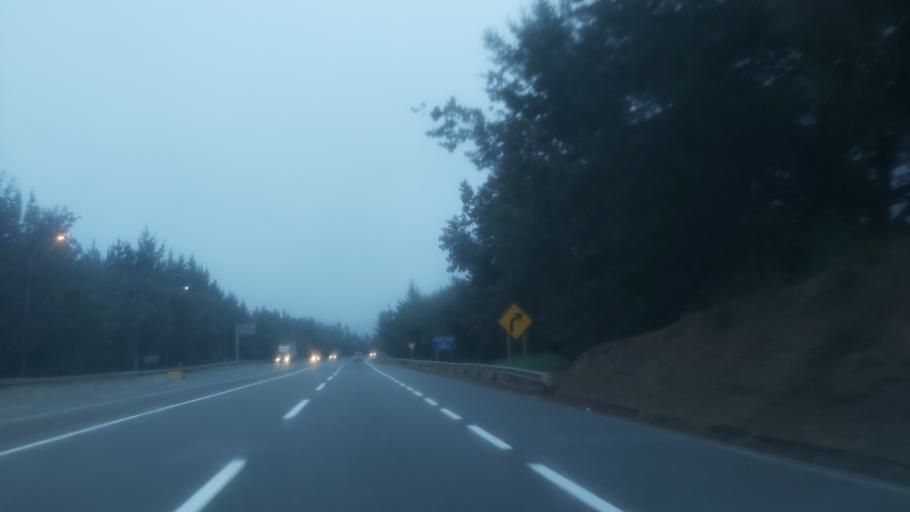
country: CL
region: Biobio
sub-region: Provincia de Concepcion
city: Penco
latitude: -36.7364
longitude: -72.8899
